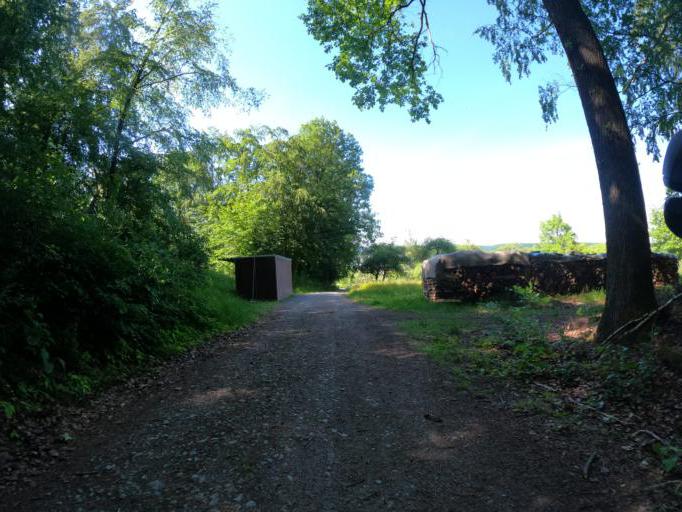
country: DE
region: Baden-Wuerttemberg
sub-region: Regierungsbezirk Stuttgart
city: Magstadt
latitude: 48.7556
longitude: 8.9869
